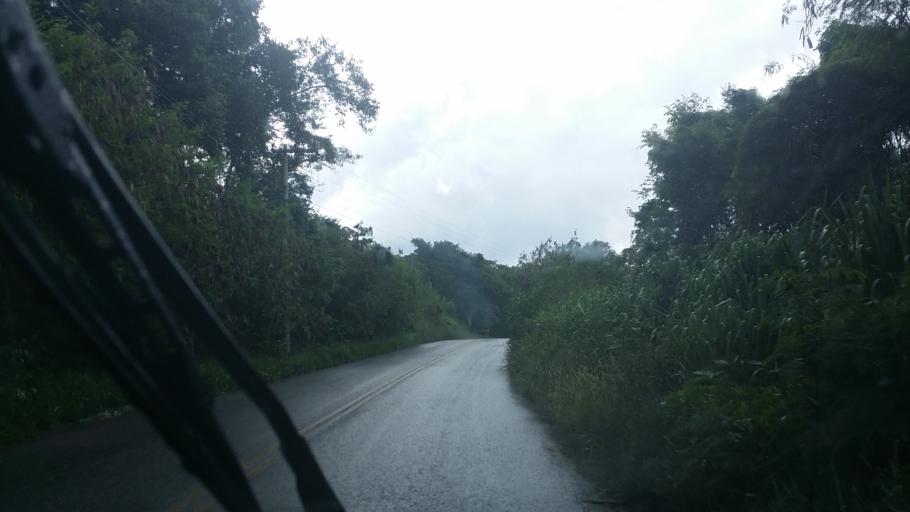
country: BR
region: Sao Paulo
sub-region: Itupeva
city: Itupeva
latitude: -23.1709
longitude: -47.1203
